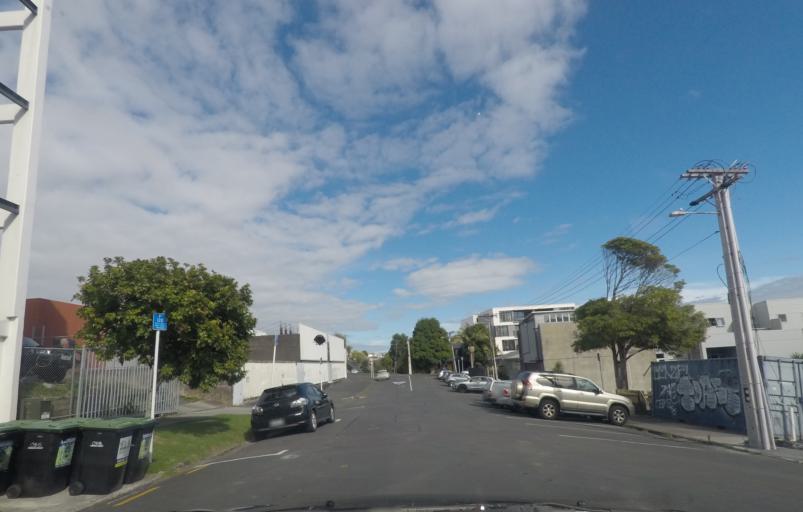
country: NZ
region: Auckland
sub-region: Auckland
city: Auckland
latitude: -36.8711
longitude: 174.7458
